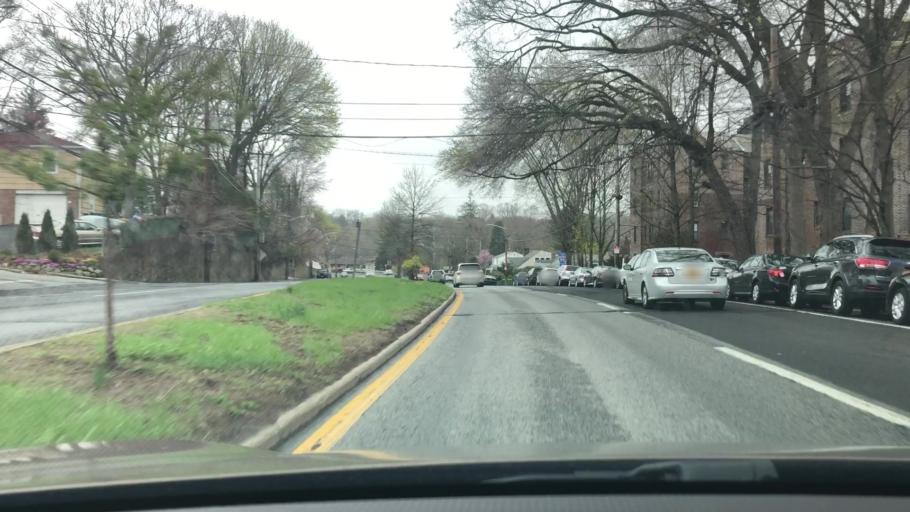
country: US
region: New York
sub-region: Westchester County
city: Mamaroneck
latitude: 40.9656
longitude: -73.7356
